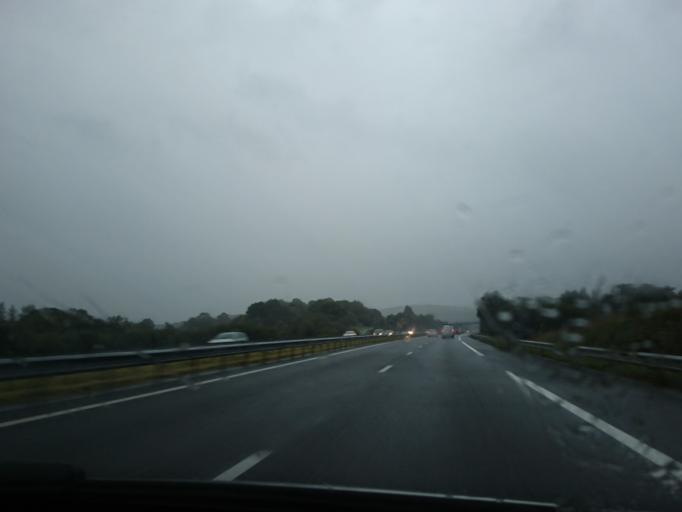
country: FR
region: Brittany
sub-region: Departement du Finistere
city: Le Faou
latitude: 48.3021
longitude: -4.1813
